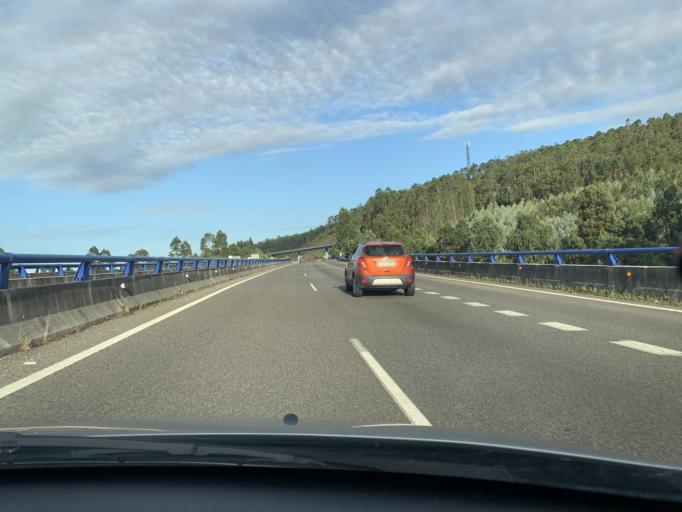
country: ES
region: Galicia
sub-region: Provincia de Lugo
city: Barreiros
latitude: 43.5356
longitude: -7.2383
